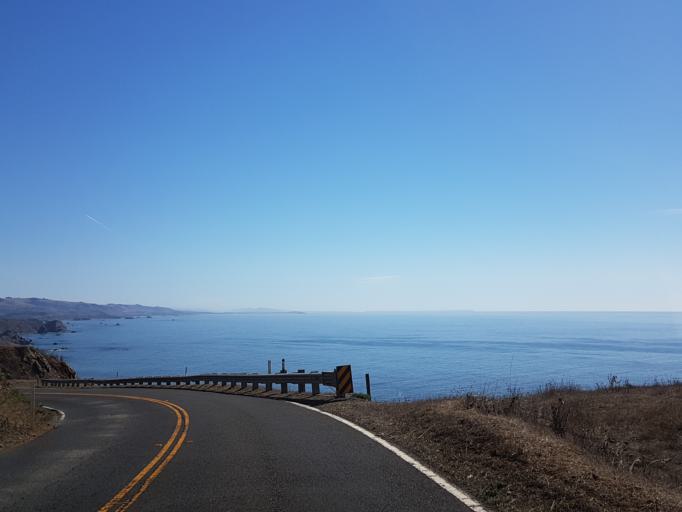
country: US
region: California
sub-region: Sonoma County
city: Monte Rio
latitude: 38.4926
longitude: -123.1965
